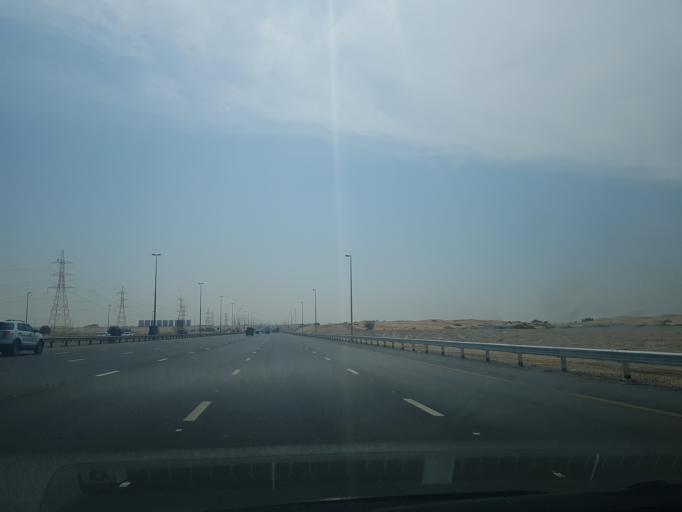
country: AE
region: Ash Shariqah
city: Sharjah
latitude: 25.2804
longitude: 55.5854
